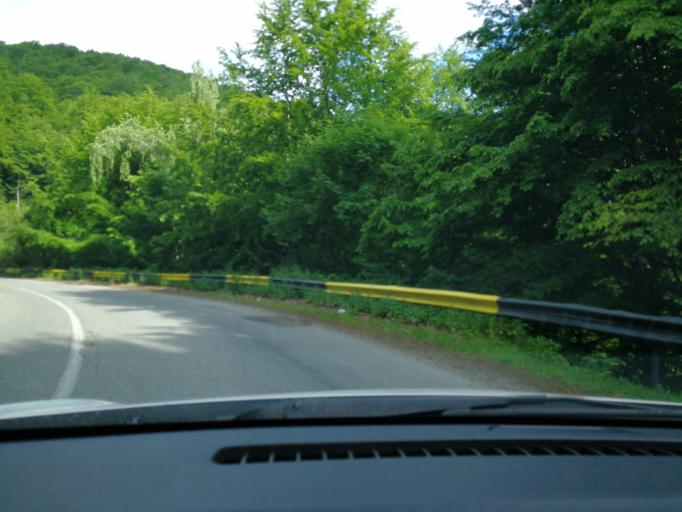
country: RO
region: Prahova
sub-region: Comuna Valea Doftanei
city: Tesila
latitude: 45.2640
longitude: 25.7332
